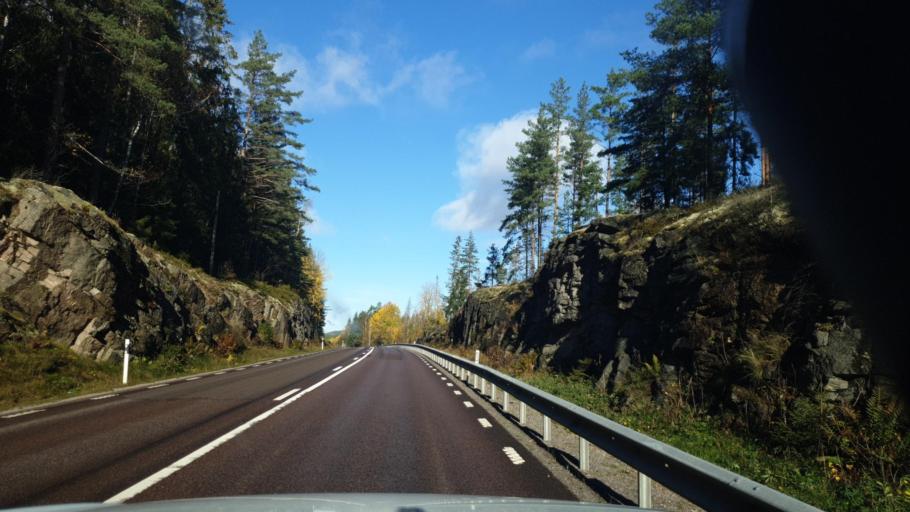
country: SE
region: Vaermland
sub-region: Karlstads Kommun
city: Edsvalla
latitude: 59.5935
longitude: 13.0083
